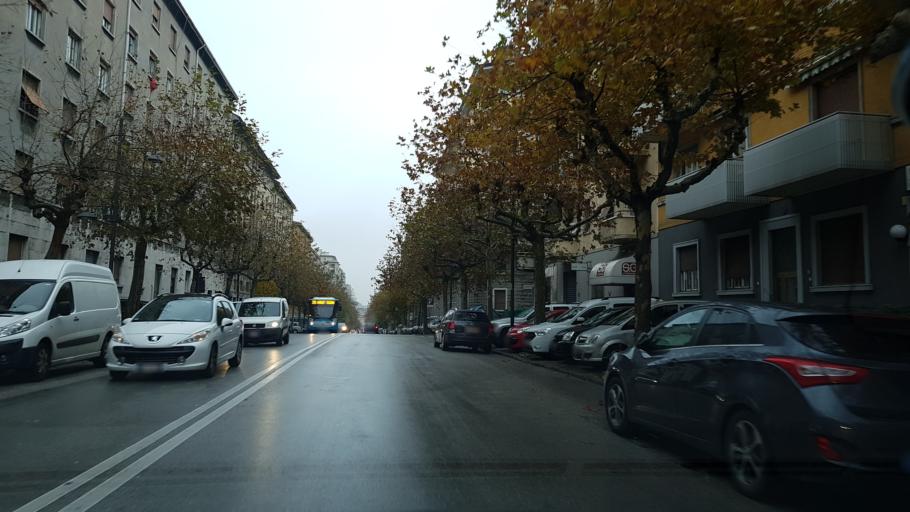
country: IT
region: Friuli Venezia Giulia
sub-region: Provincia di Trieste
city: Trieste
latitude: 45.6404
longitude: 13.7877
